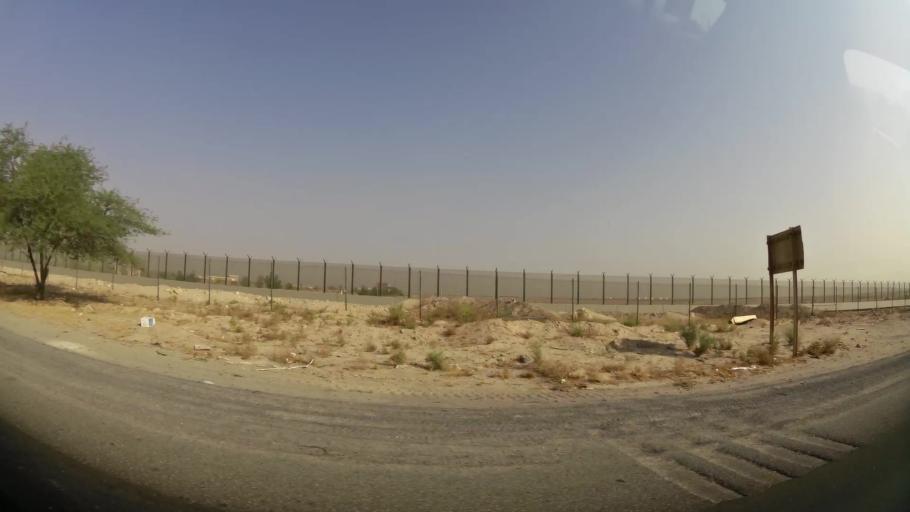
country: KW
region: Al Farwaniyah
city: Janub as Surrah
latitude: 29.1822
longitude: 47.9718
